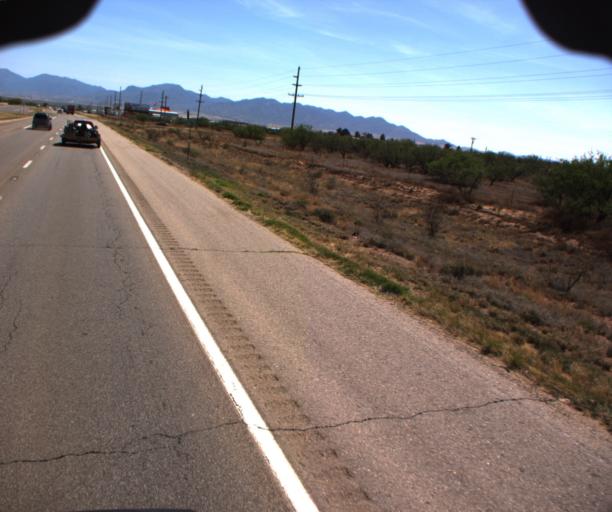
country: US
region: Arizona
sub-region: Cochise County
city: Huachuca City
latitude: 31.6887
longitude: -110.3505
